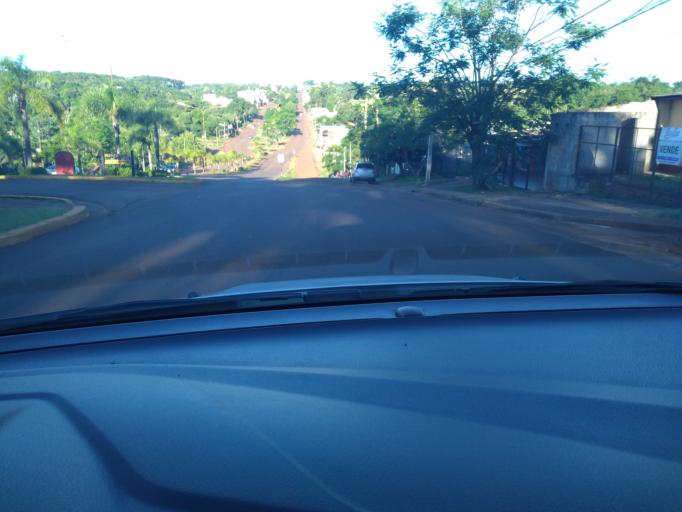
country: AR
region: Misiones
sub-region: Departamento de Obera
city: Obera
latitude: -27.4806
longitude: -55.1086
